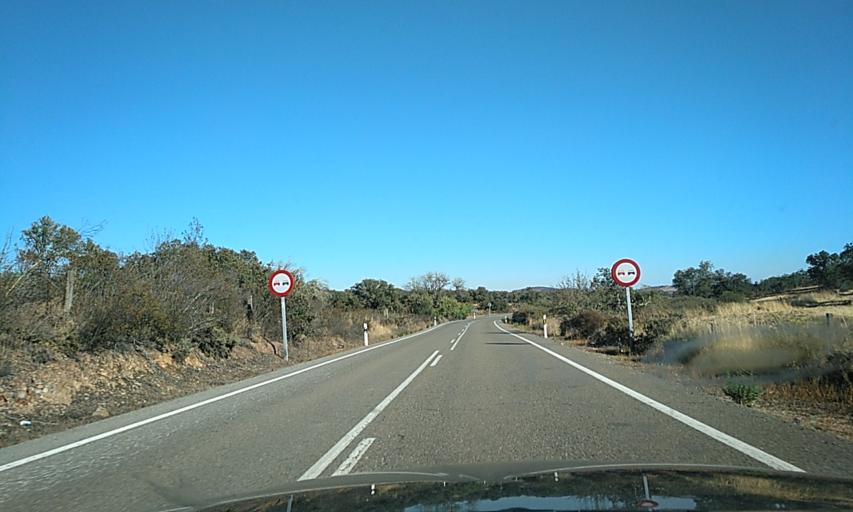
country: ES
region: Andalusia
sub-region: Provincia de Huelva
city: Cabezas Rubias
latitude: 37.7622
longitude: -7.1355
